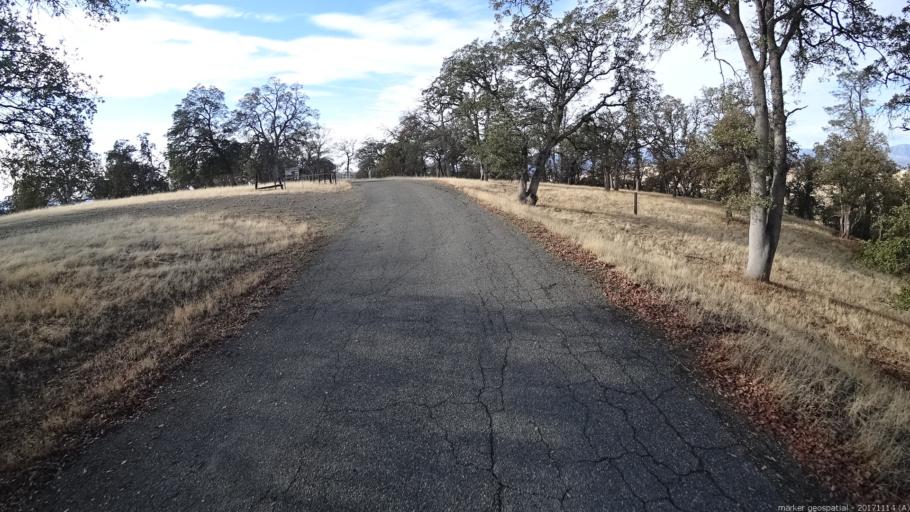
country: US
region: California
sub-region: Shasta County
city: Shasta
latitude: 40.3821
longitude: -122.5905
